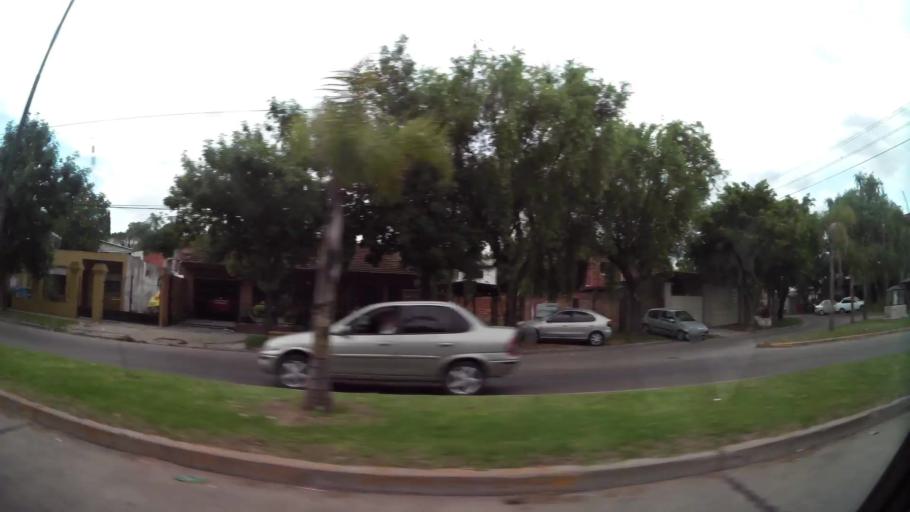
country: AR
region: Buenos Aires
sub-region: Partido de Tigre
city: Tigre
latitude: -34.4774
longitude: -58.5787
